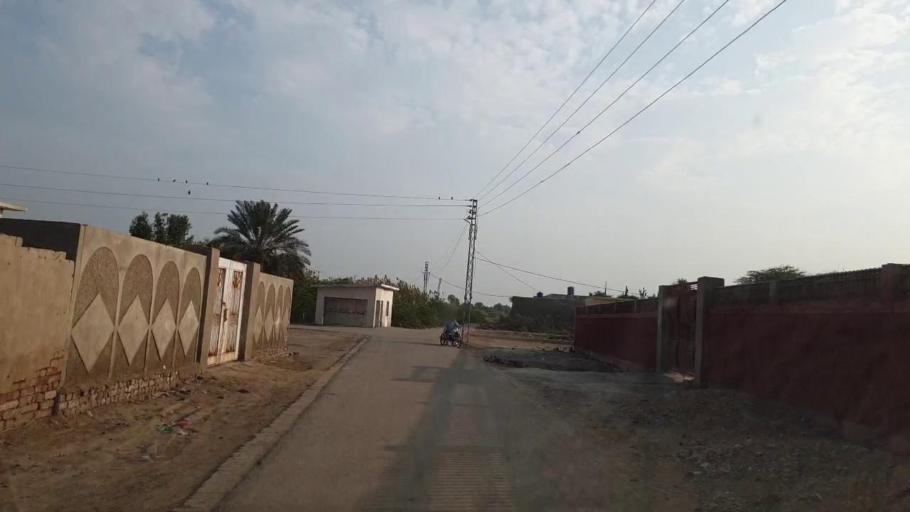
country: PK
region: Sindh
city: Pithoro
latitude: 25.5826
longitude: 69.3619
